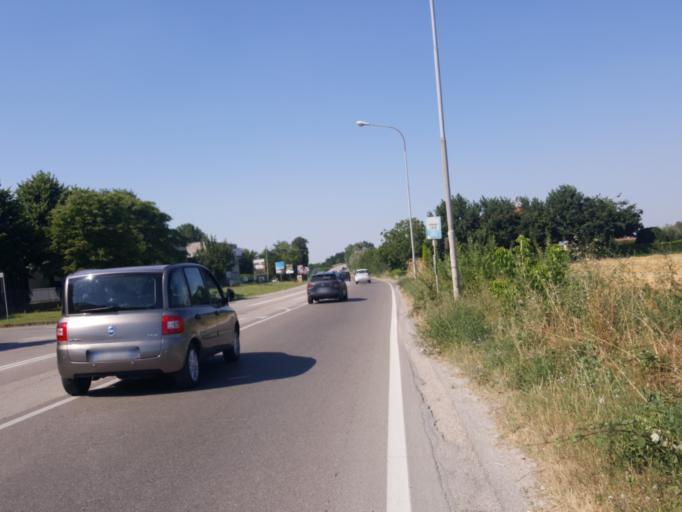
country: IT
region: Emilia-Romagna
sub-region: Provincia di Bologna
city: Castel San Pietro Terme
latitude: 44.4046
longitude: 11.5877
